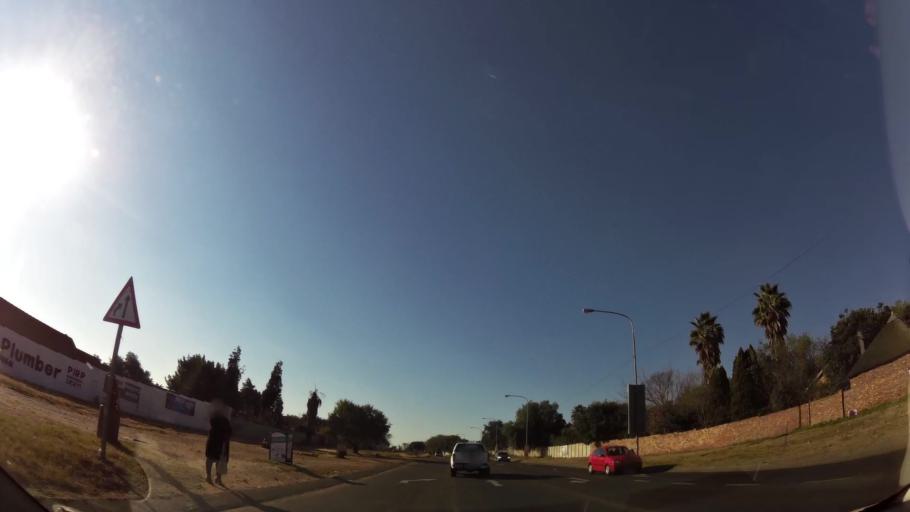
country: ZA
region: Gauteng
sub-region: City of Tshwane Metropolitan Municipality
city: Centurion
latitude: -25.8936
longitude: 28.1422
